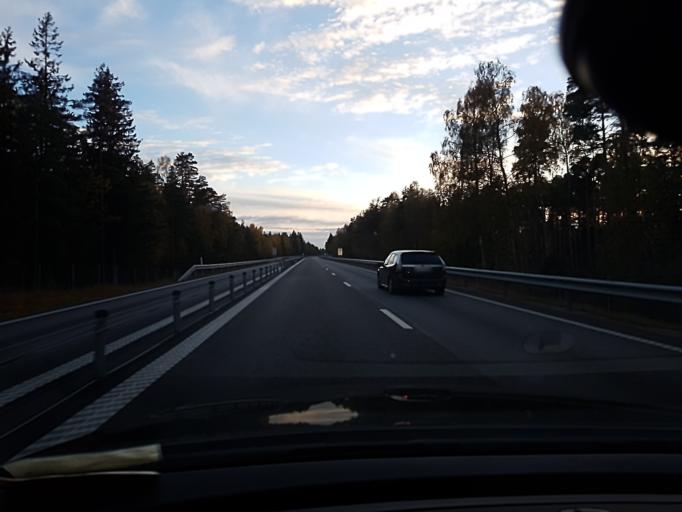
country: SE
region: Kronoberg
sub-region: Ljungby Kommun
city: Ljungby
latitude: 56.7790
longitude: 13.8171
